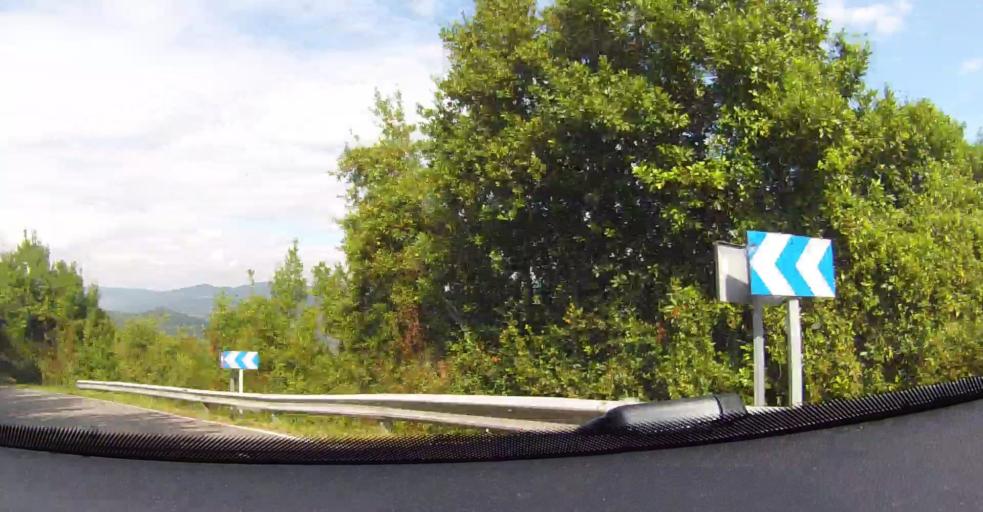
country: ES
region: Asturias
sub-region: Province of Asturias
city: Villaviciosa
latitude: 43.4864
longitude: -5.4203
